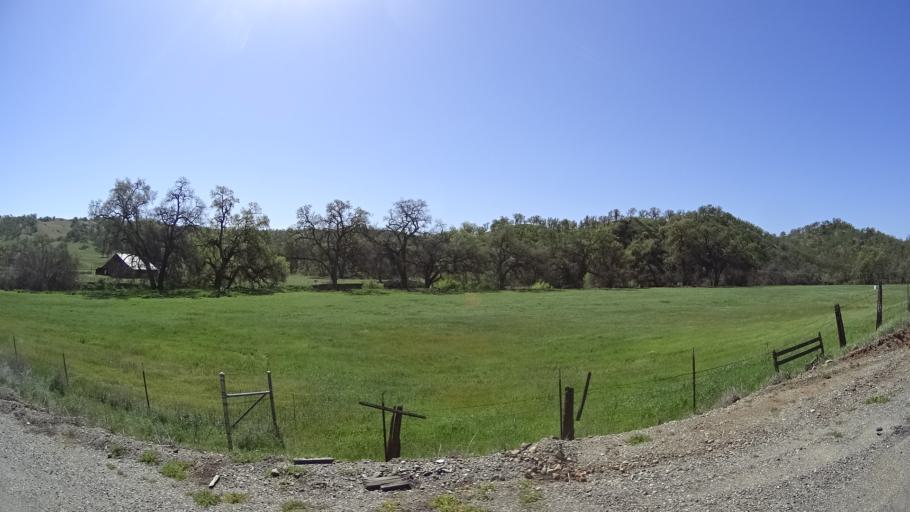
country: US
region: California
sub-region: Tehama County
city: Rancho Tehama Reserve
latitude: 39.7856
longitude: -122.4779
